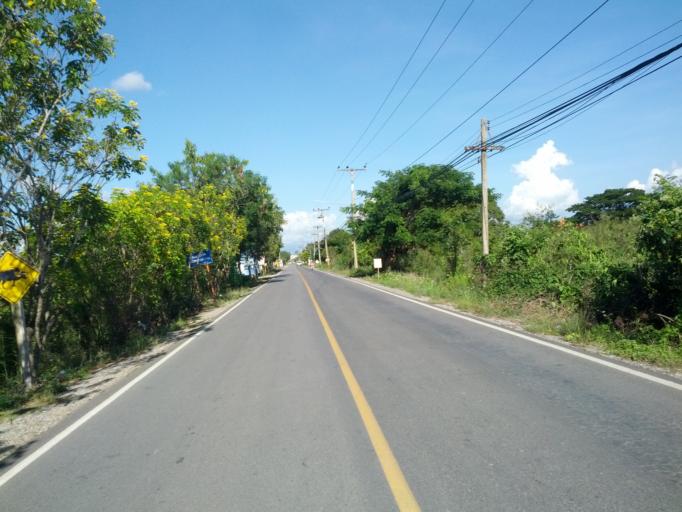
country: TH
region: Chiang Mai
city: Saraphi
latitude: 18.7004
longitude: 99.0171
